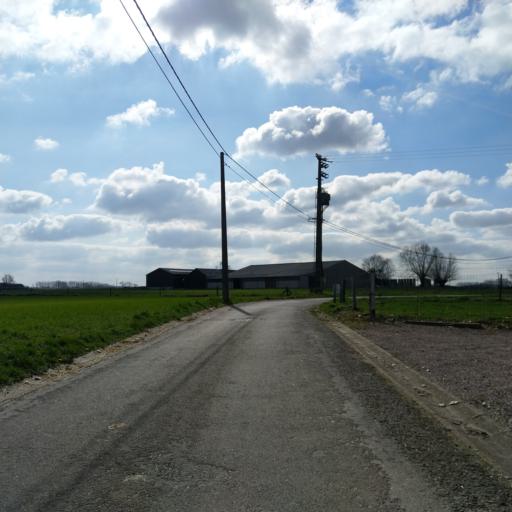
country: BE
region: Wallonia
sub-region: Province du Hainaut
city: Lens
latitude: 50.5588
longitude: 3.9421
